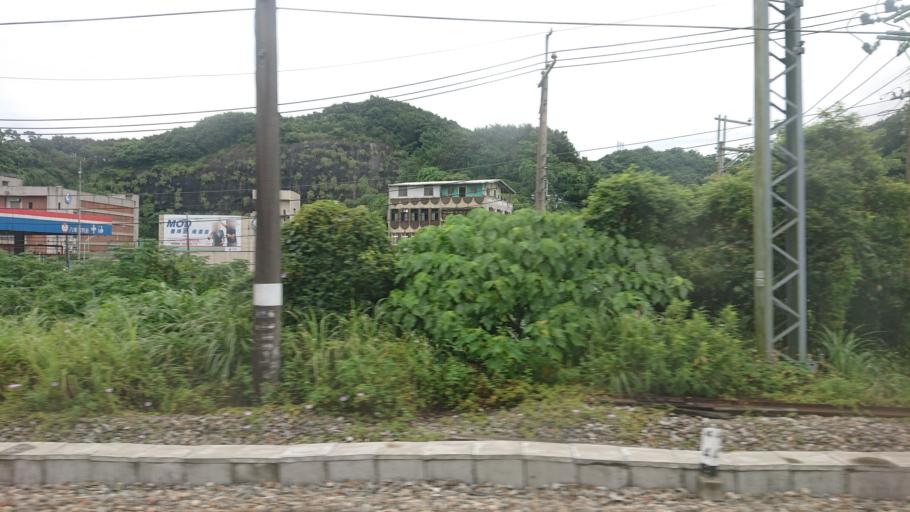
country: TW
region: Taiwan
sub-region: Keelung
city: Keelung
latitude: 25.1031
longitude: 121.7253
